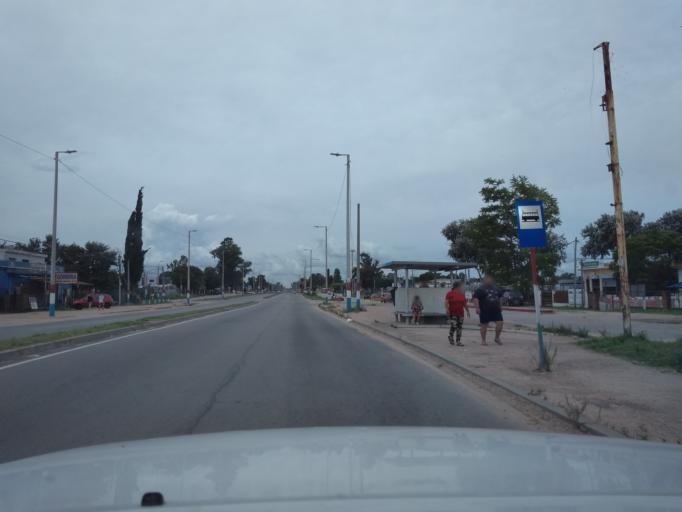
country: UY
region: Canelones
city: Paso de Carrasco
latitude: -34.8634
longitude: -56.0560
